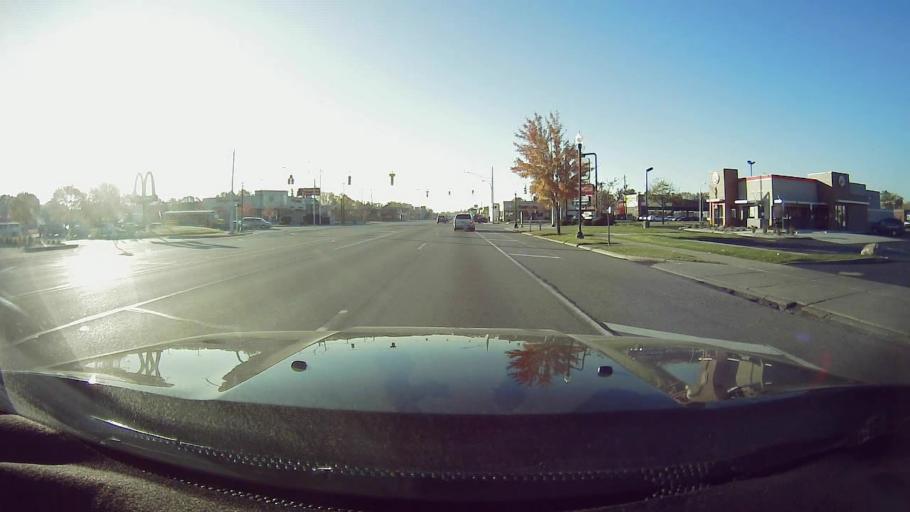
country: US
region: Michigan
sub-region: Macomb County
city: Warren
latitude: 42.4641
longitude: -83.0268
